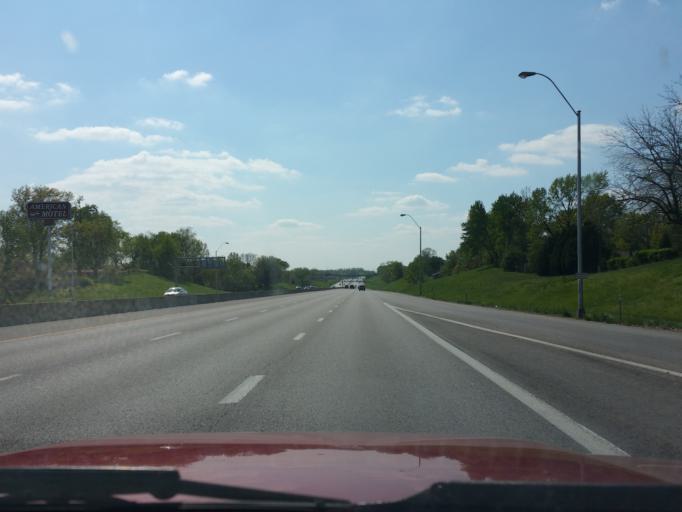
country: US
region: Kansas
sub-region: Wyandotte County
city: Edwardsville
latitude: 39.1052
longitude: -94.7634
